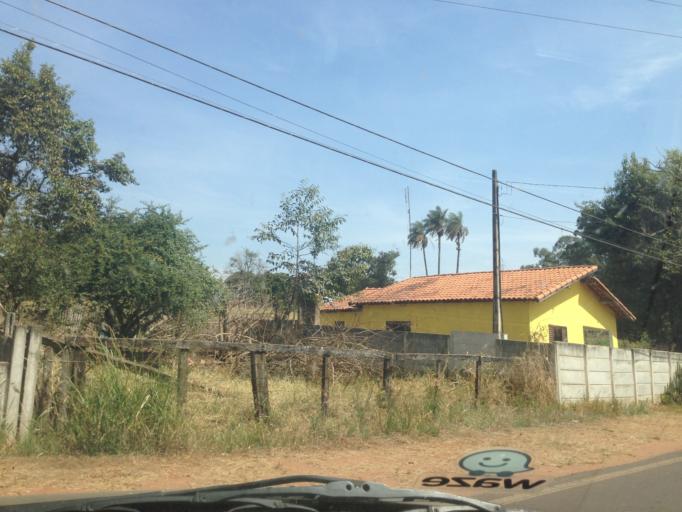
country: BR
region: Sao Paulo
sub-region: Casa Branca
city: Casa Branca
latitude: -21.7692
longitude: -47.0960
